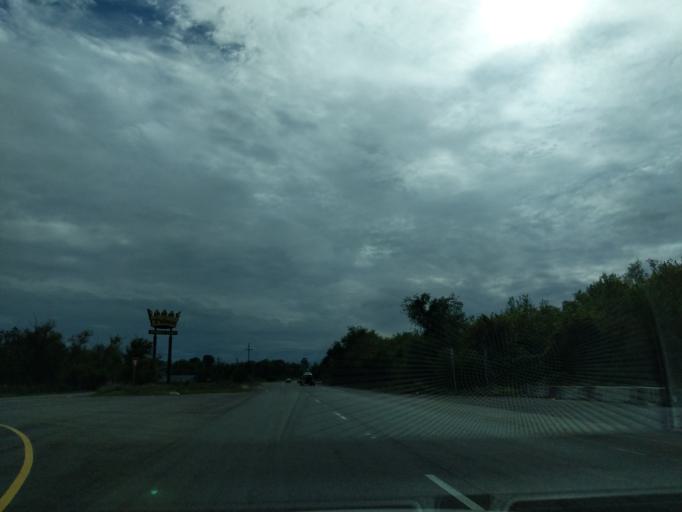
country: US
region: Louisiana
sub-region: Saint Bernard Parish
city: Chalmette
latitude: 30.0148
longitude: -89.9447
